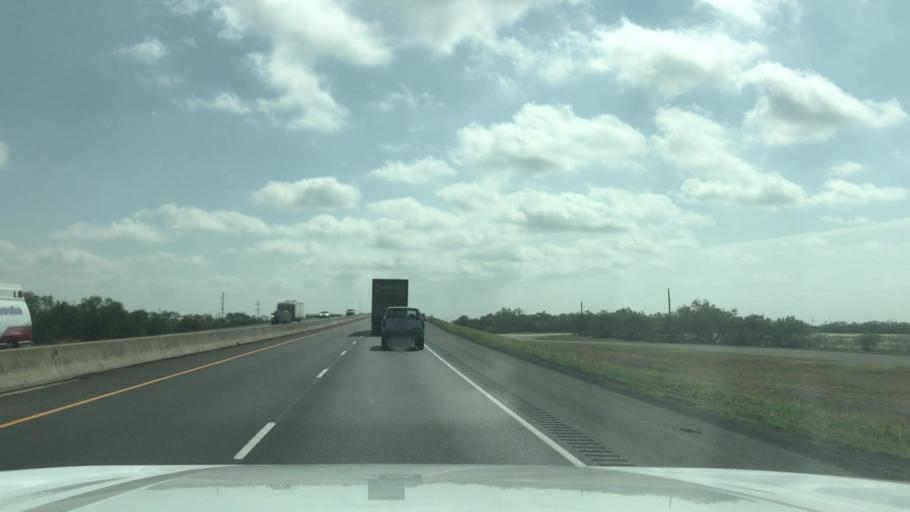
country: US
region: Texas
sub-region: Taylor County
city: Merkel
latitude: 32.4936
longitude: -100.1524
